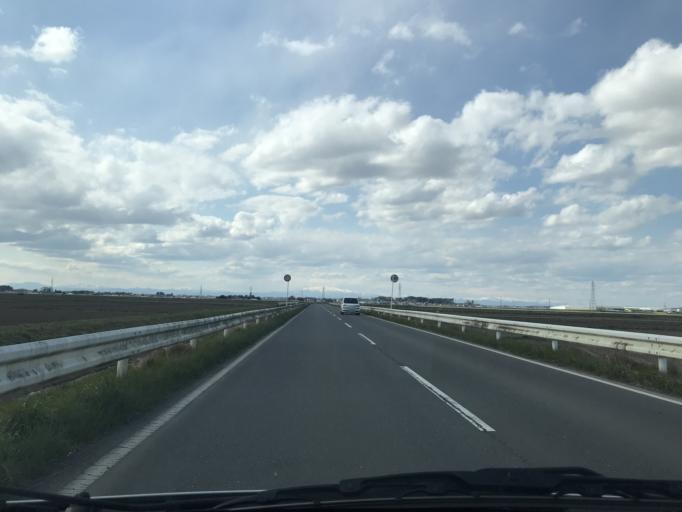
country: JP
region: Miyagi
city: Wakuya
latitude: 38.6514
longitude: 141.2408
